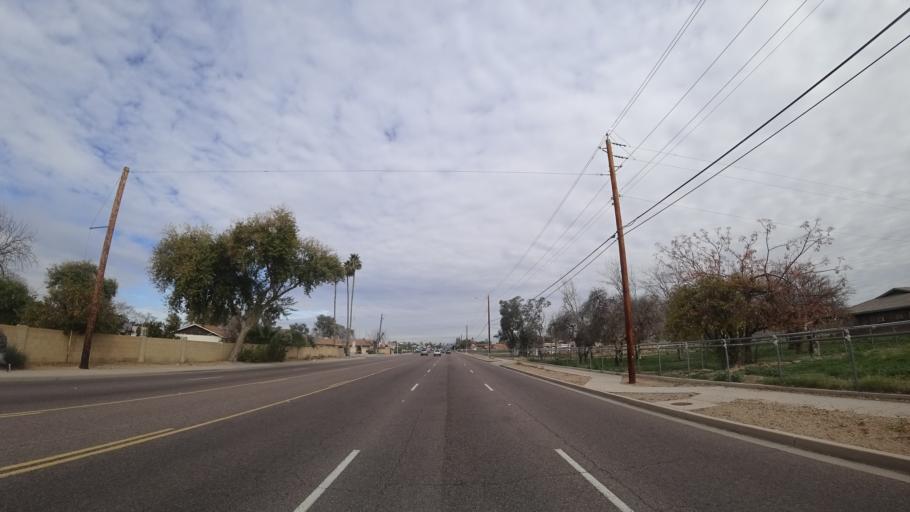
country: US
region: Arizona
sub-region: Maricopa County
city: Glendale
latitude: 33.5790
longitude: -112.1688
